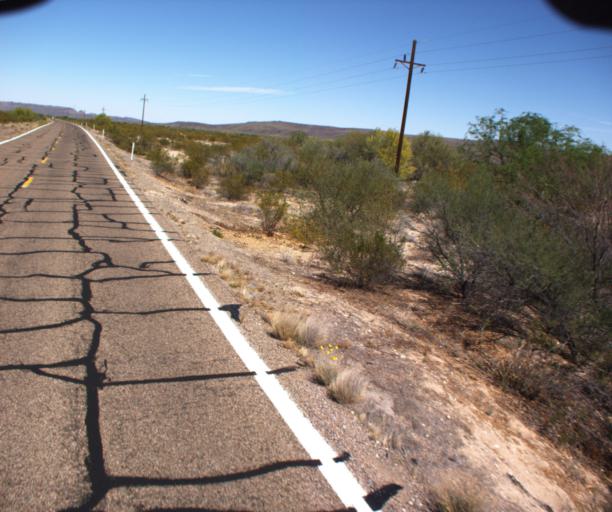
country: US
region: Arizona
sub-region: Pima County
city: Ajo
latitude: 32.4582
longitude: -112.8725
